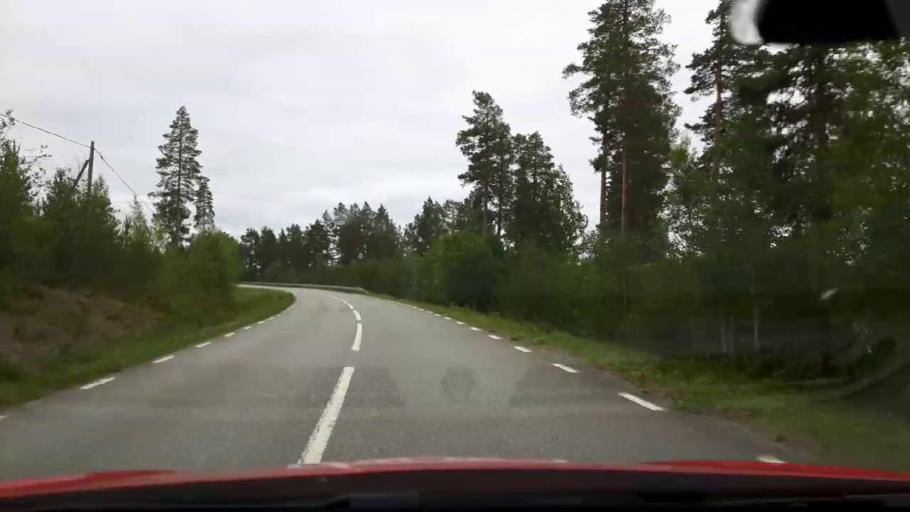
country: SE
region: Jaemtland
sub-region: Stroemsunds Kommun
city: Stroemsund
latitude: 63.3746
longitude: 15.6945
